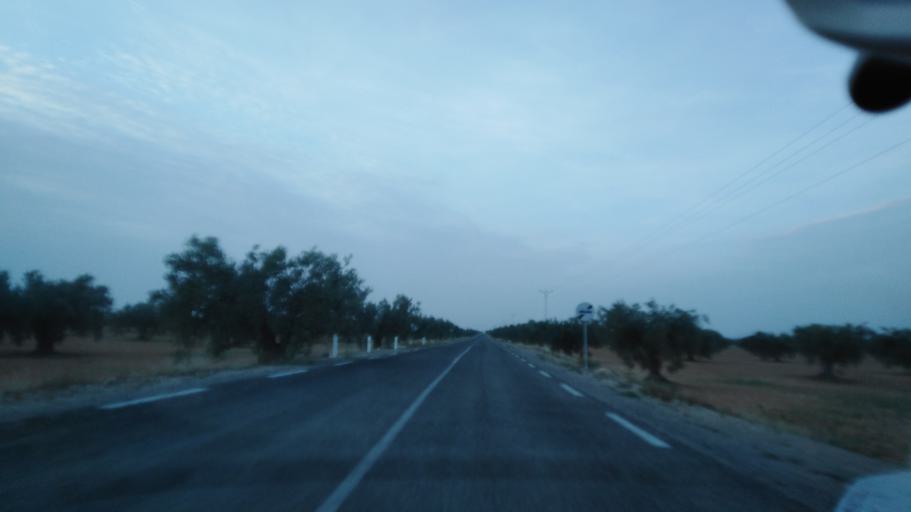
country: TN
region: Safaqis
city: Bi'r `Ali Bin Khalifah
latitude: 34.9036
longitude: 10.3879
